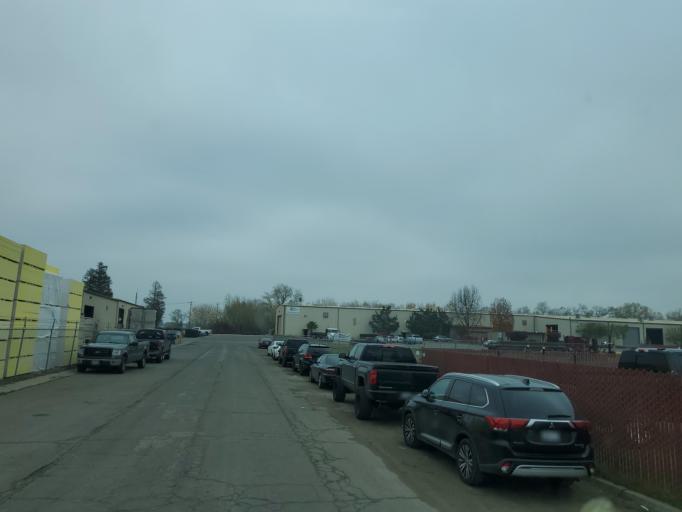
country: US
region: California
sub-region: San Joaquin County
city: Lathrop
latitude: 37.8214
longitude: -121.2655
